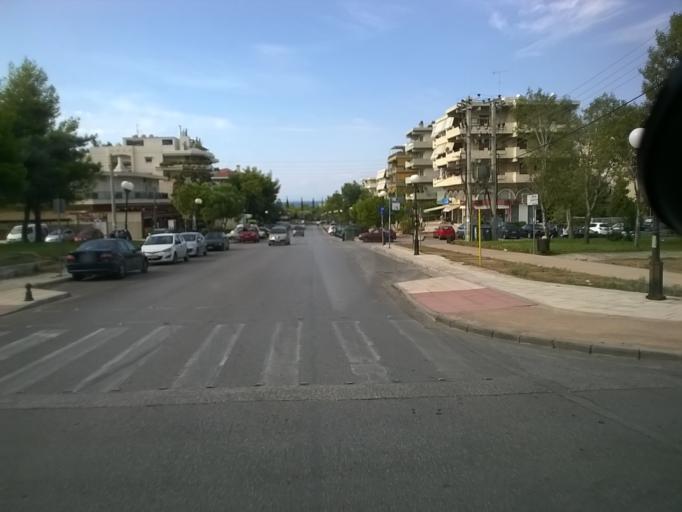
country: GR
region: Attica
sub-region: Nomarchia Anatolikis Attikis
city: Voula
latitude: 37.8488
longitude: 23.7661
